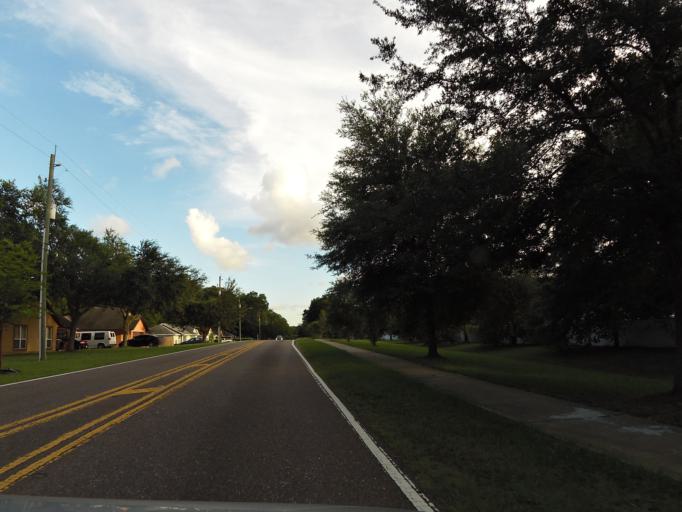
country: US
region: Florida
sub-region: Duval County
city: Jacksonville
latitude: 30.4090
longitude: -81.6974
